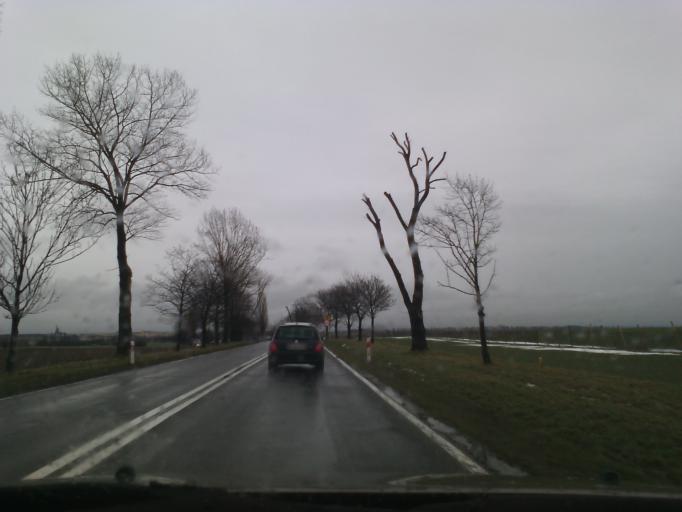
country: PL
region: Lower Silesian Voivodeship
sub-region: Powiat swidnicki
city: Swidnica
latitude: 50.8376
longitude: 16.4116
